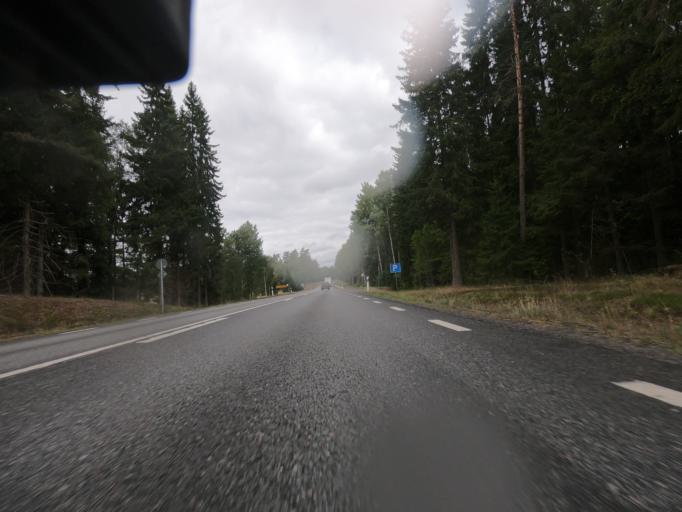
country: SE
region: Joenkoeping
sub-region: Vaggeryds Kommun
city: Vaggeryd
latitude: 57.4566
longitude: 14.3158
